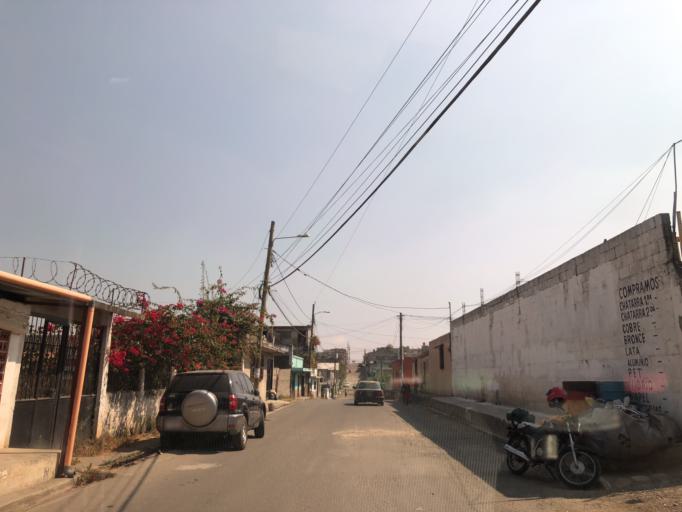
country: GT
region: Guatemala
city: Amatitlan
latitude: 14.5060
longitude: -90.6018
